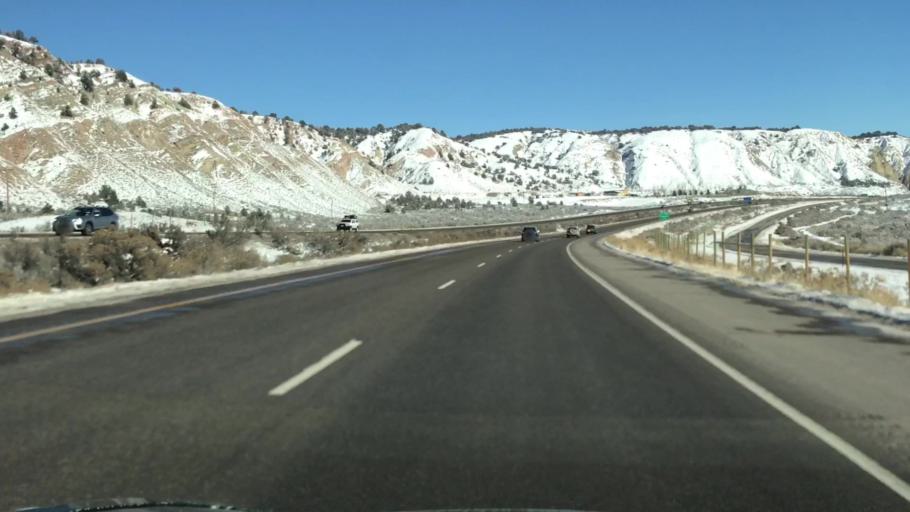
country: US
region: Colorado
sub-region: Eagle County
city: Gypsum
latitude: 39.6556
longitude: -106.9789
